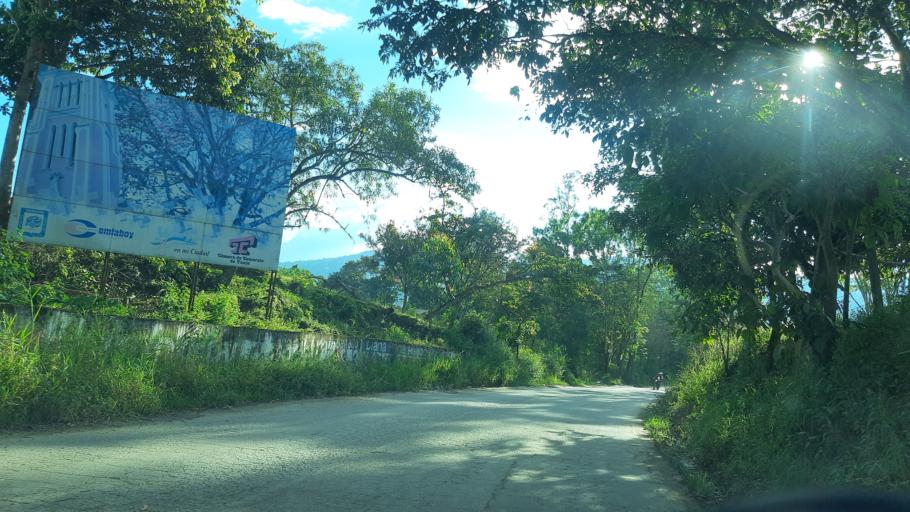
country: CO
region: Boyaca
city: Garagoa
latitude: 5.0764
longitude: -73.3752
